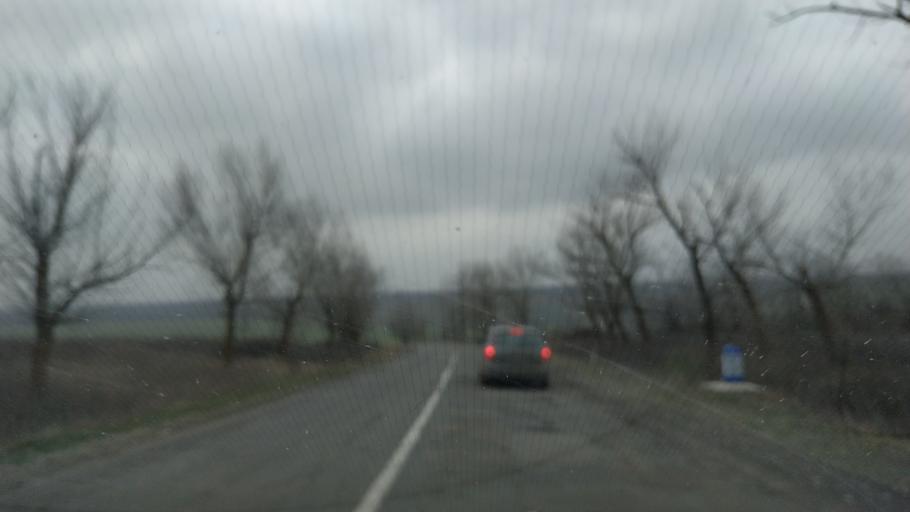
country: MD
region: Gagauzia
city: Bugeac
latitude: 46.3376
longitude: 28.7621
